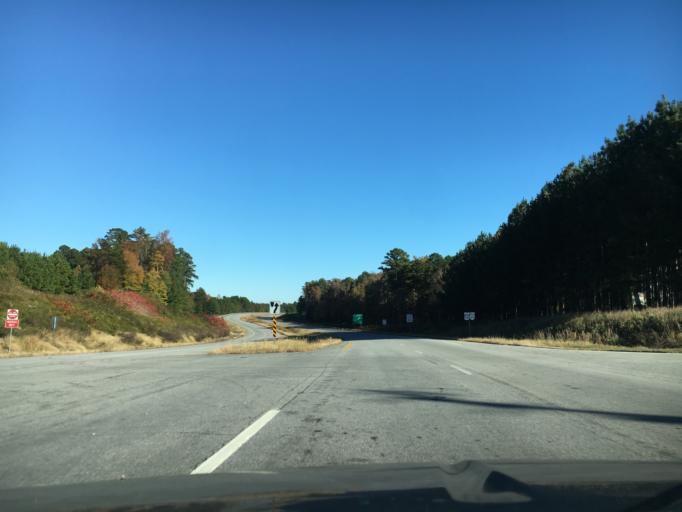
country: US
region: Virginia
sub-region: Mecklenburg County
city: Clarksville
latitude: 36.6110
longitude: -78.5867
